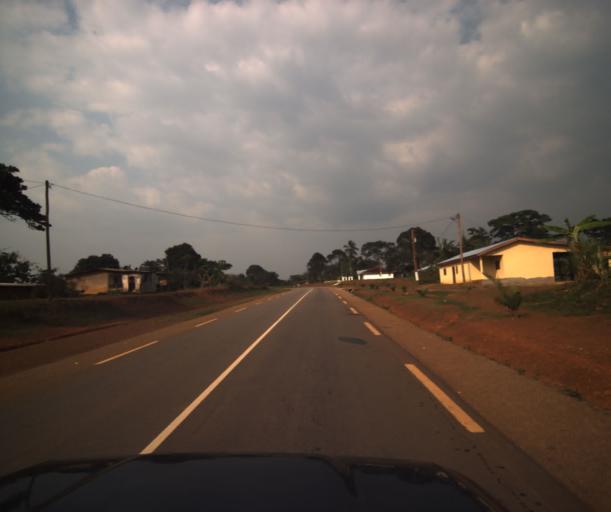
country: CM
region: Centre
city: Mbankomo
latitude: 3.7075
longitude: 11.3785
